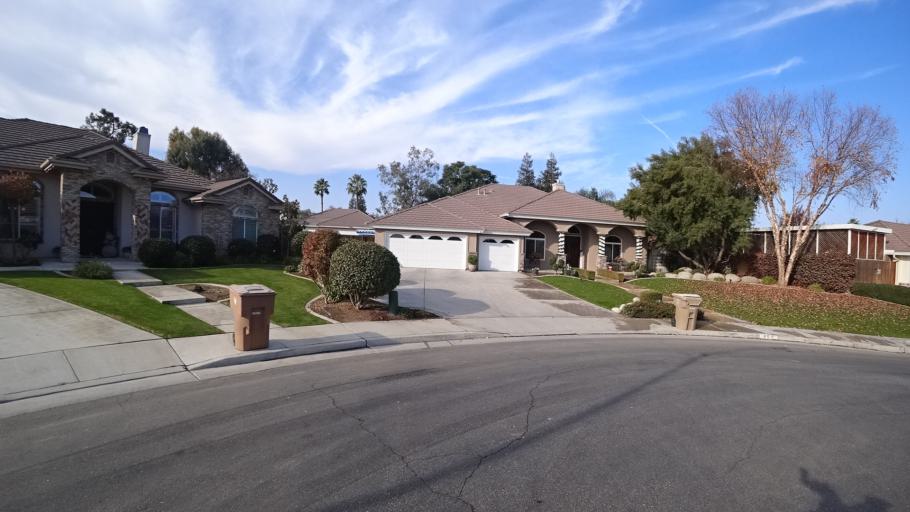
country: US
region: California
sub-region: Kern County
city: Rosedale
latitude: 35.3657
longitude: -119.1567
